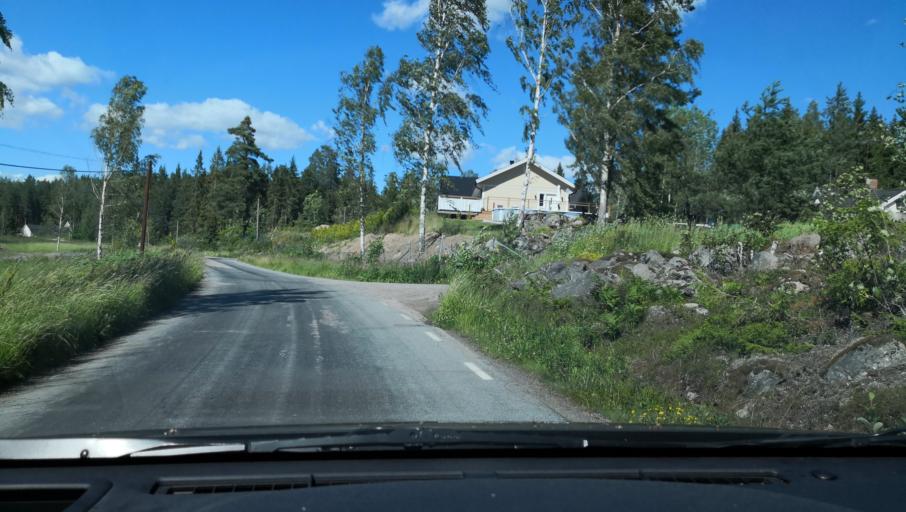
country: SE
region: Soedermanland
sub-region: Eskilstuna Kommun
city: Hallbybrunn
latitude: 59.3142
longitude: 16.3785
